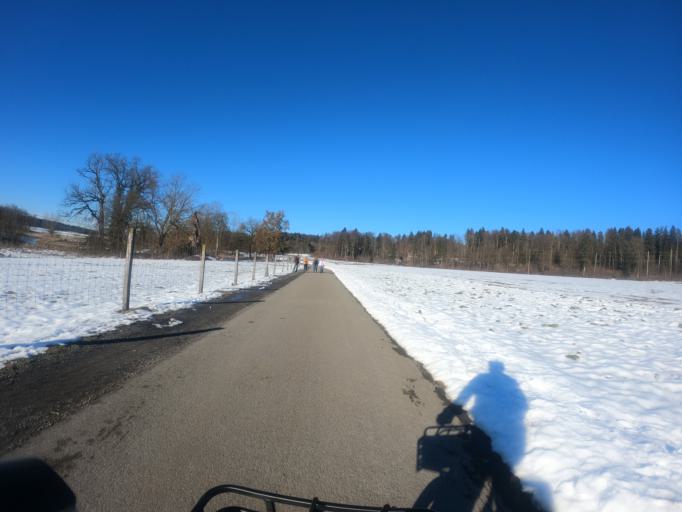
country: CH
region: Aargau
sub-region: Bezirk Bremgarten
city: Unterlunkhofen
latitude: 47.3306
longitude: 8.3676
